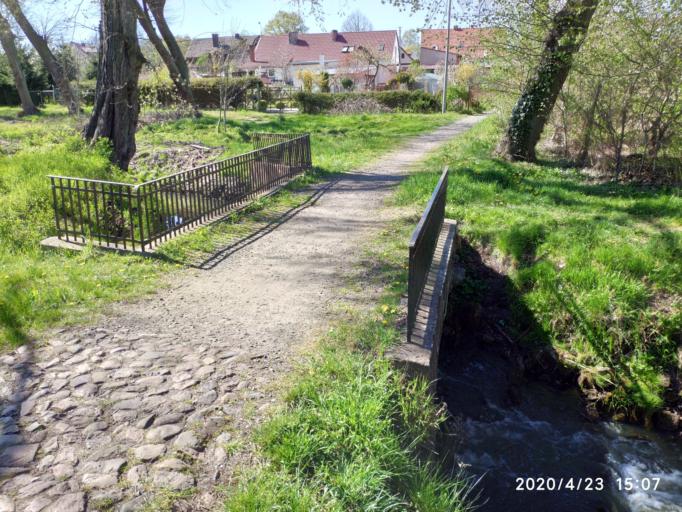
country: PL
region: Lubusz
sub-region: Powiat slubicki
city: Osno Lubuskie
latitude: 52.4562
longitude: 14.8675
